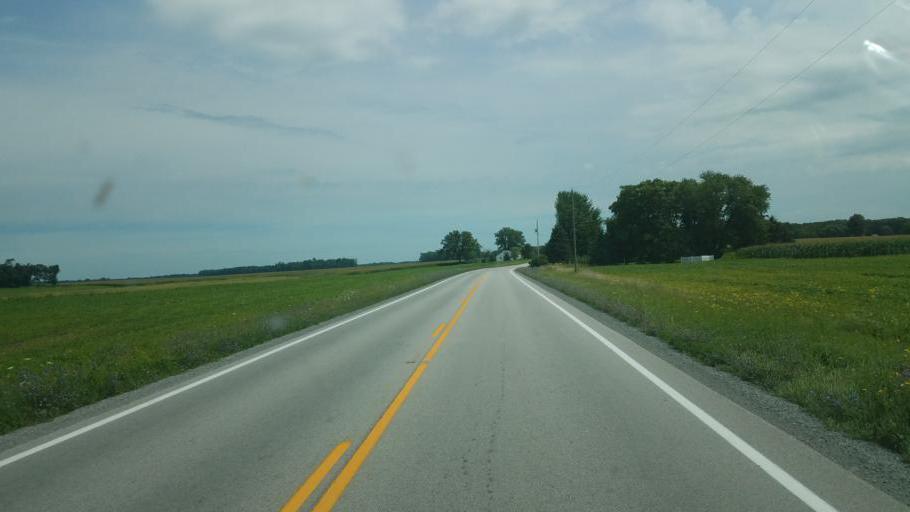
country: US
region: Ohio
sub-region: Wyandot County
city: Upper Sandusky
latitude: 40.8665
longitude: -83.2623
